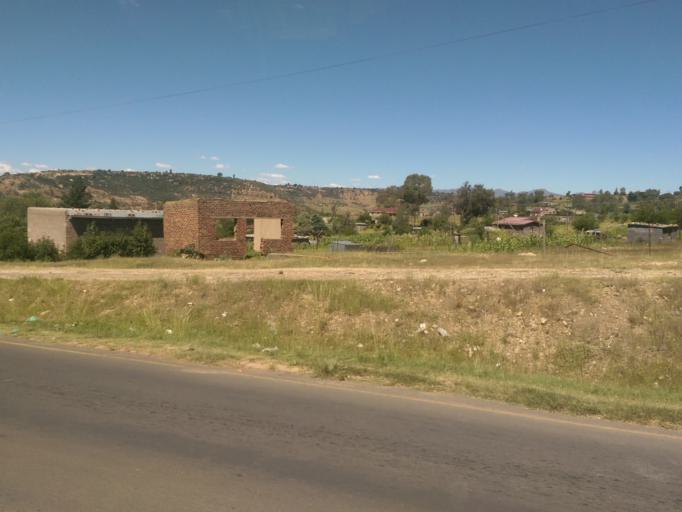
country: LS
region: Maseru
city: Maseru
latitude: -29.4122
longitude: 27.5585
